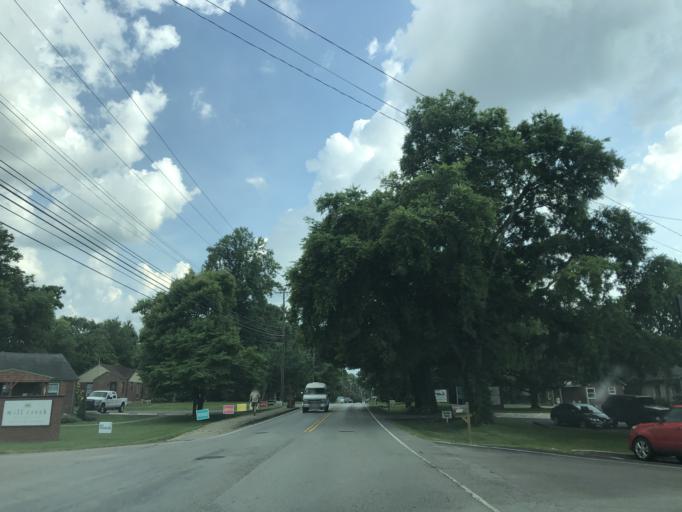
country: US
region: Tennessee
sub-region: Davidson County
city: Lakewood
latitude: 36.1683
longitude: -86.6800
